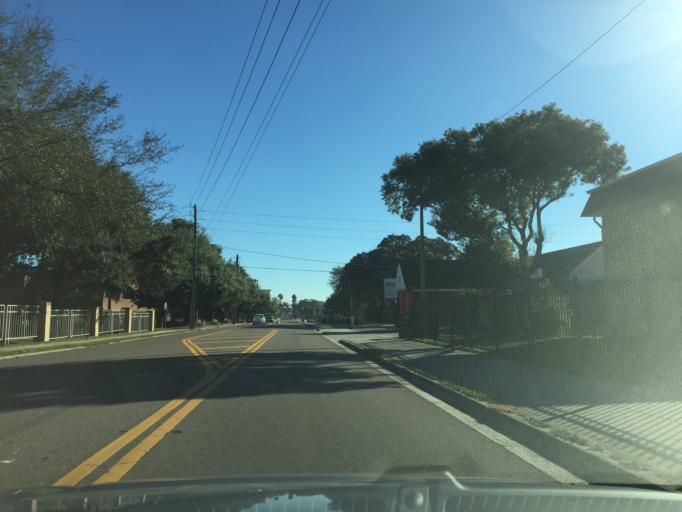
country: US
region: Florida
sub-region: Hillsborough County
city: Tampa
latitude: 27.9603
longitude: -82.4494
